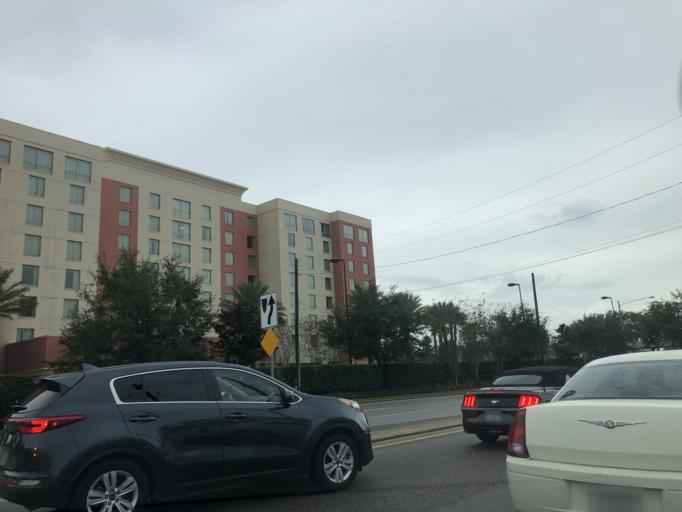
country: US
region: Florida
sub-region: Orange County
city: Doctor Phillips
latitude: 28.4516
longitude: -81.4777
